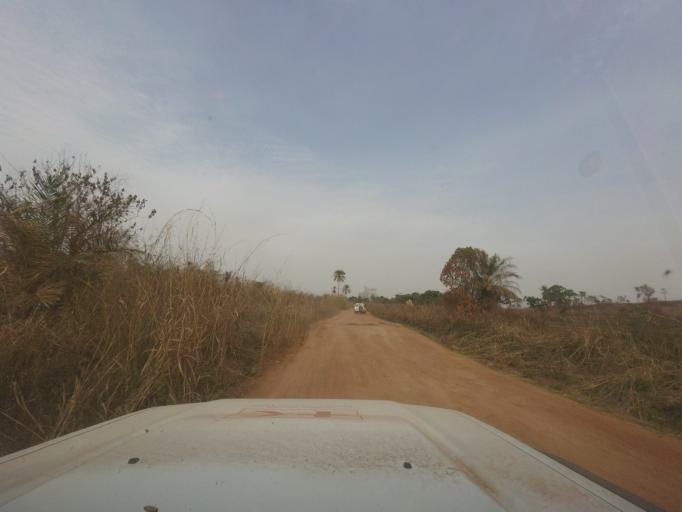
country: GN
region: Nzerekore
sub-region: Prefecture de Guekedou
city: Gueckedou
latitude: 8.5200
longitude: -10.1992
